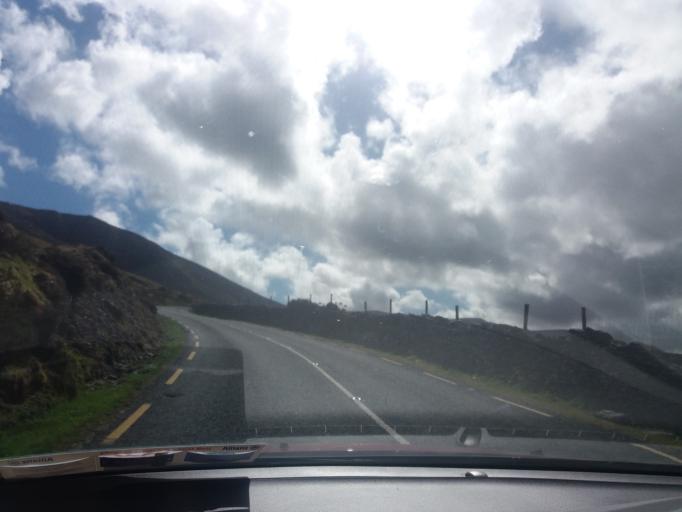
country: IE
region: Munster
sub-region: Ciarrai
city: Dingle
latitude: 52.2009
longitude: -10.1782
